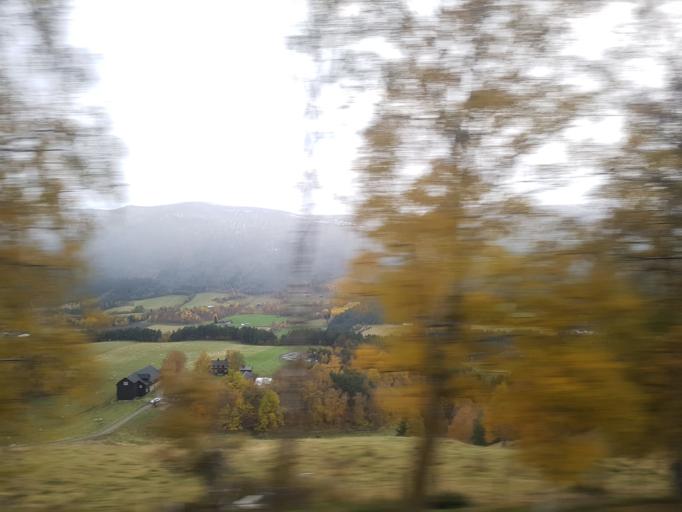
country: NO
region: Oppland
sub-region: Dovre
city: Dovre
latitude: 62.0219
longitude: 9.1899
